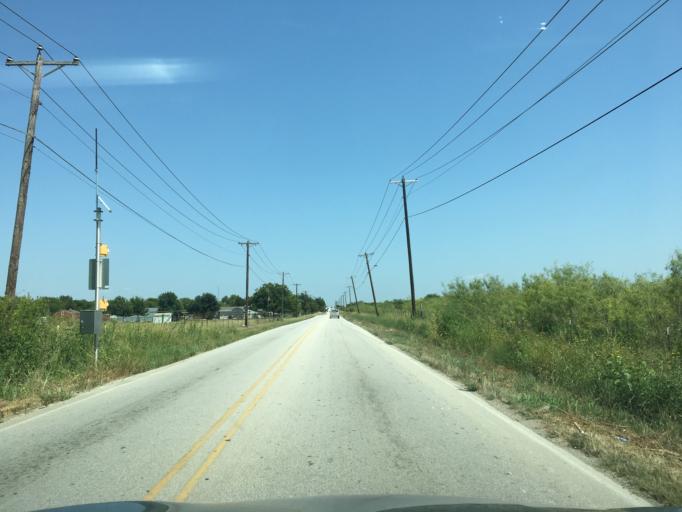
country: US
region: Texas
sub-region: Tarrant County
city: Crowley
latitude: 32.6141
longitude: -97.3462
